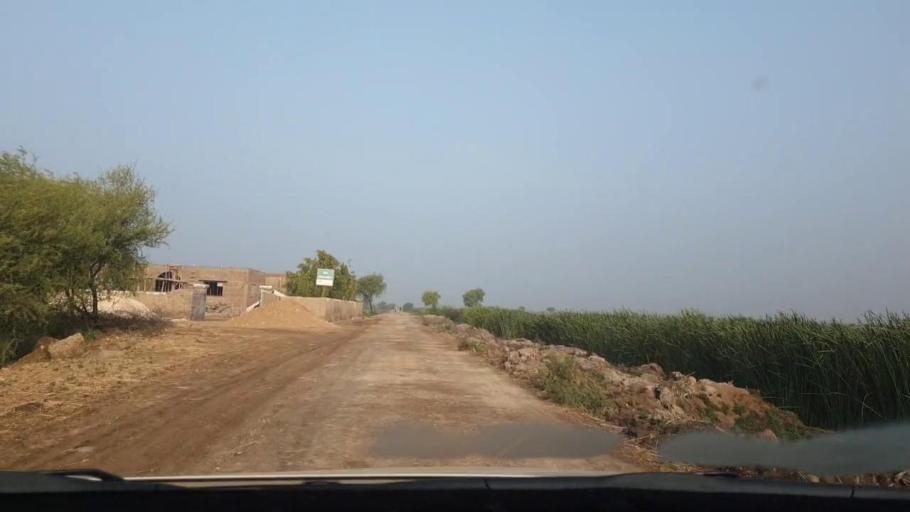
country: PK
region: Sindh
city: Tando Muhammad Khan
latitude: 25.0886
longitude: 68.4822
